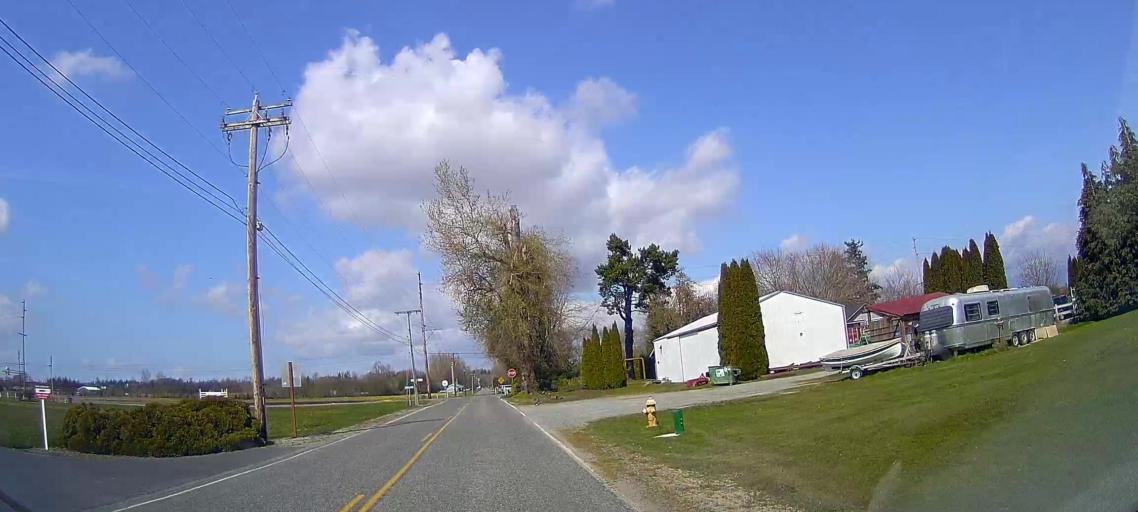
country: US
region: Washington
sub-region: Skagit County
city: Mount Vernon
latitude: 48.4419
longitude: -122.4220
